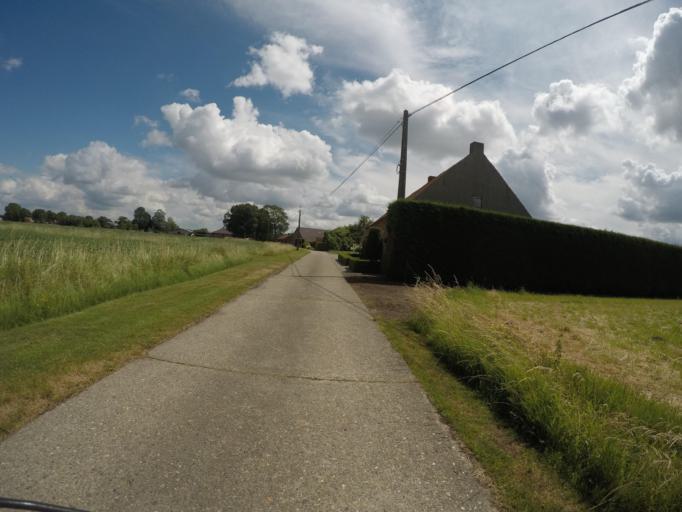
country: BE
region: Flanders
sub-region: Provincie Antwerpen
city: Brecht
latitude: 51.3573
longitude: 4.6841
